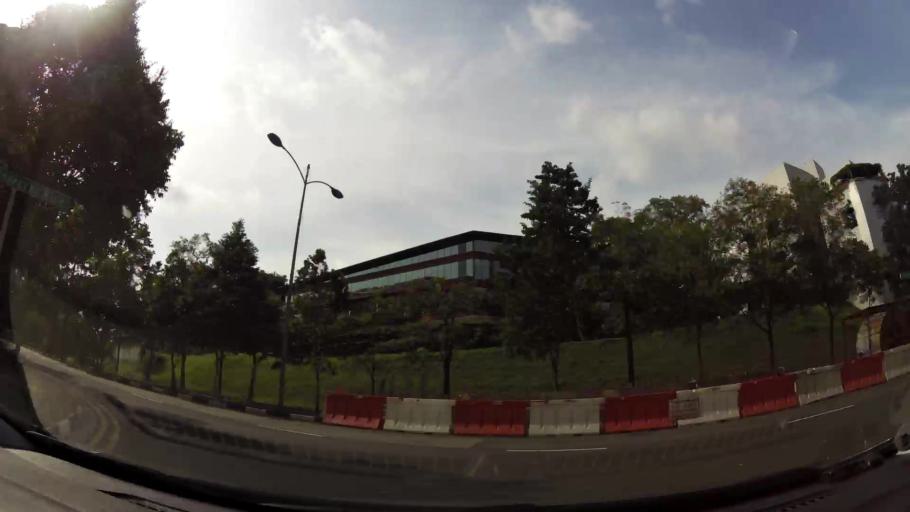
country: SG
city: Singapore
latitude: 1.3032
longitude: 103.7884
